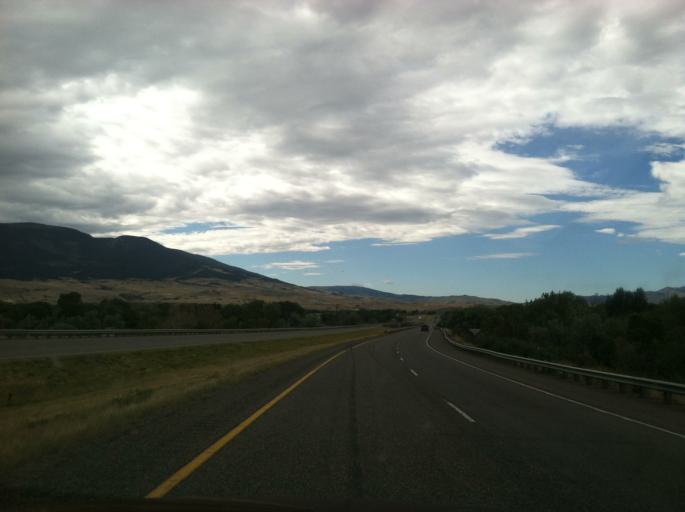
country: US
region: Montana
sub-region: Park County
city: Livingston
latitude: 45.6445
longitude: -110.5575
